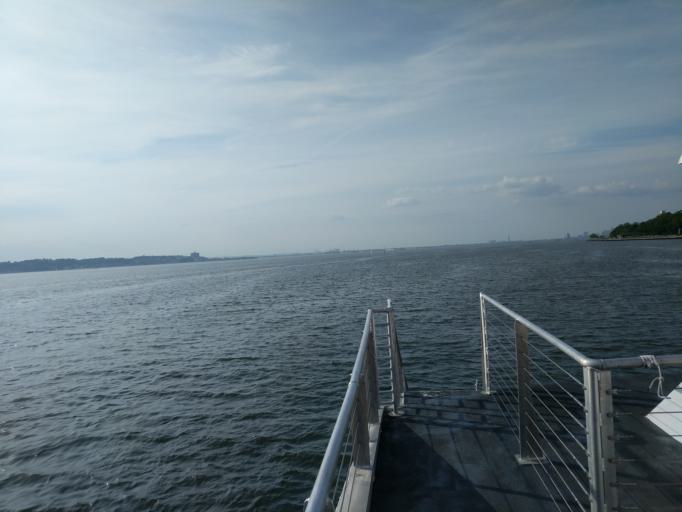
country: US
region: New York
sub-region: Kings County
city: Bensonhurst
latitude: 40.6125
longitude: -74.0421
